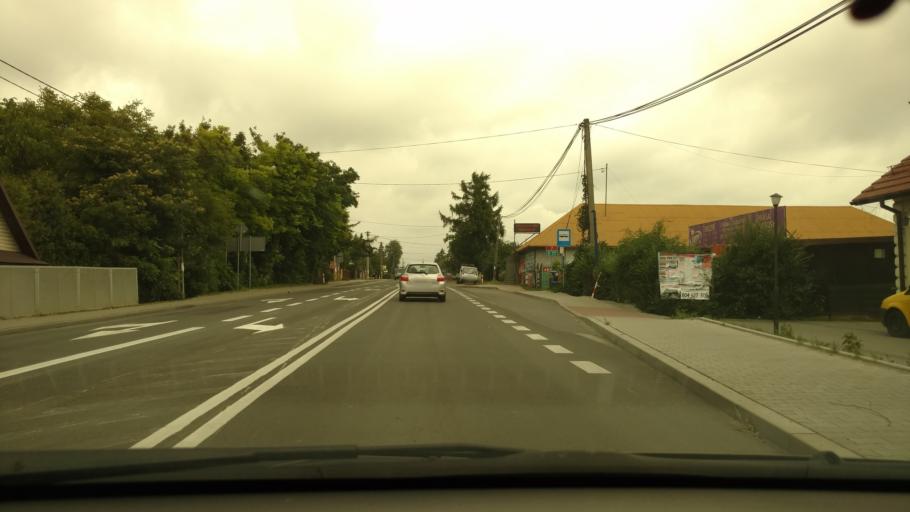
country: PL
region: Lesser Poland Voivodeship
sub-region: Powiat krakowski
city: Michalowice
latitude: 50.1202
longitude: 19.9672
